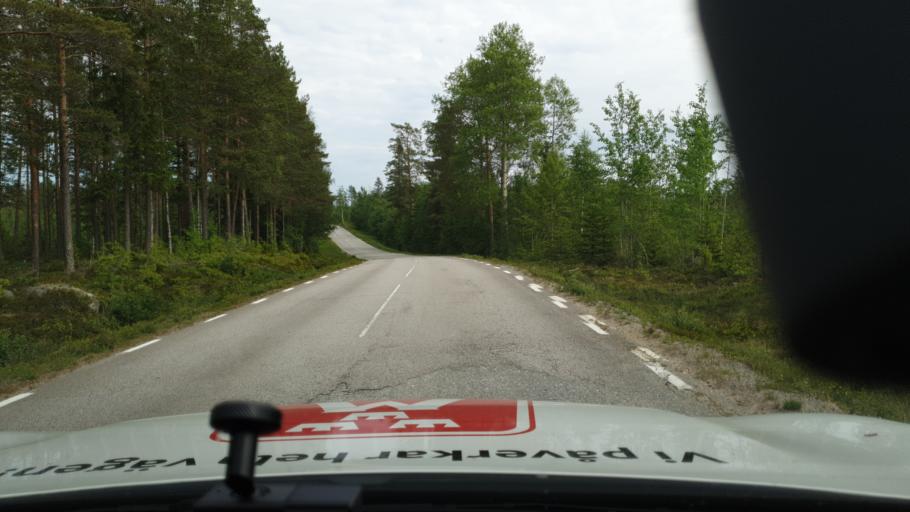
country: SE
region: Vaesterbotten
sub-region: Umea Kommun
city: Hoernefors
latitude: 63.5611
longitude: 19.7436
